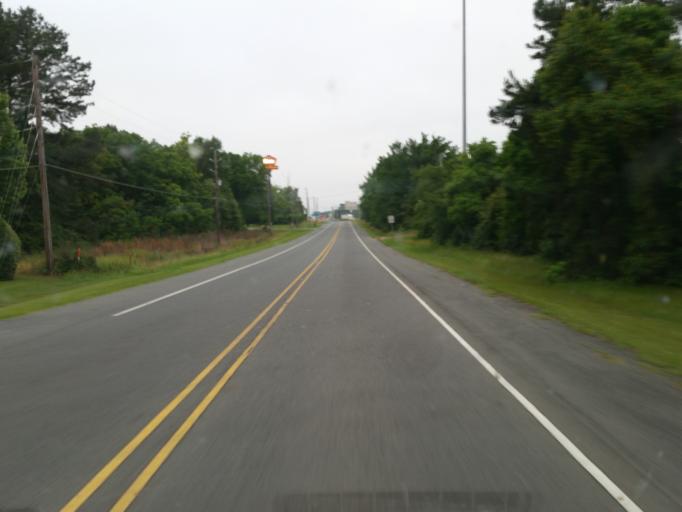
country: US
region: Louisiana
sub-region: Caddo Parish
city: Shreveport
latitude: 32.4538
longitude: -93.8482
